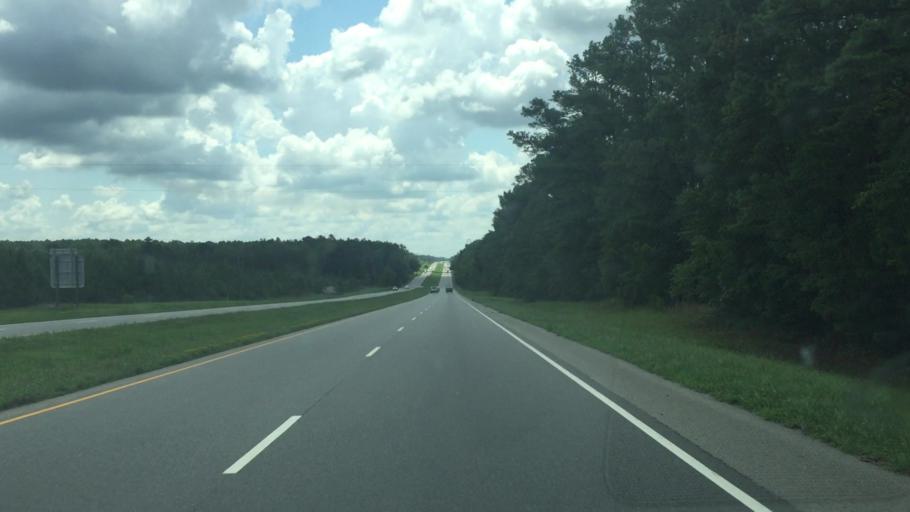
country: US
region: North Carolina
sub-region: Richmond County
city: Hamlet
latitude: 34.8603
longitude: -79.6318
